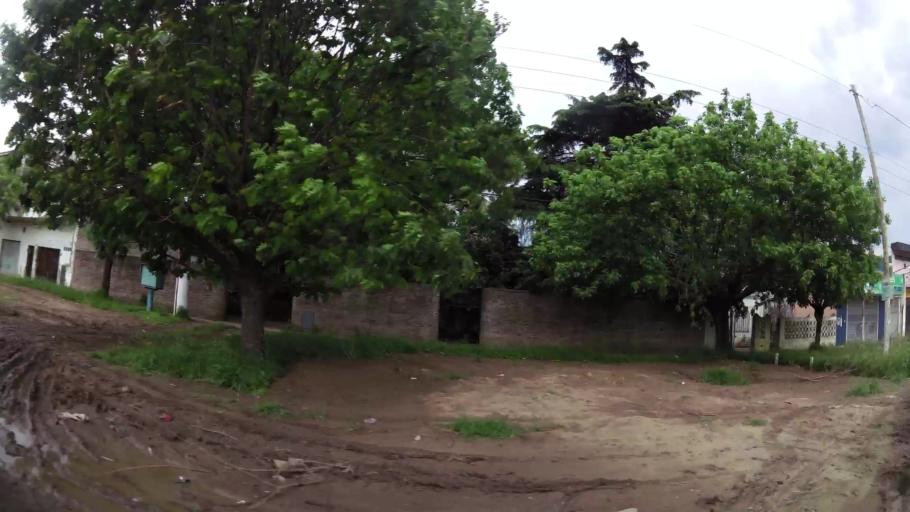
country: AR
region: Buenos Aires
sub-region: Partido de Quilmes
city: Quilmes
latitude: -34.7723
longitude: -58.2824
